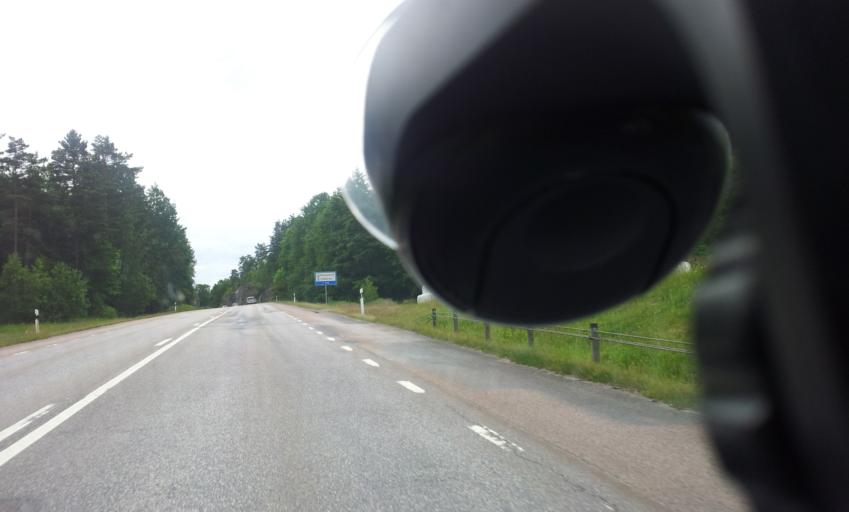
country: SE
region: Kalmar
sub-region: Vasterviks Kommun
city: Ankarsrum
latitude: 57.6711
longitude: 16.4422
